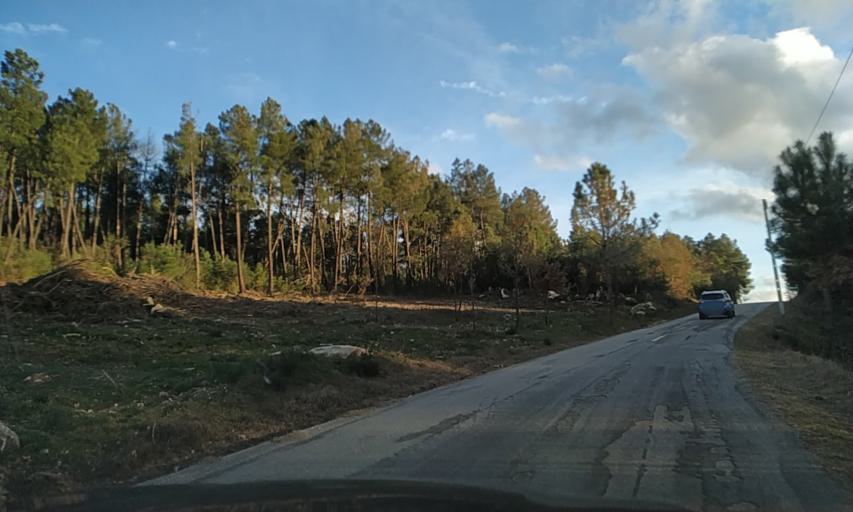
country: PT
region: Braganca
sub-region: Carrazeda de Ansiaes
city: Carrazeda de Anciaes
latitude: 41.2282
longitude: -7.3385
